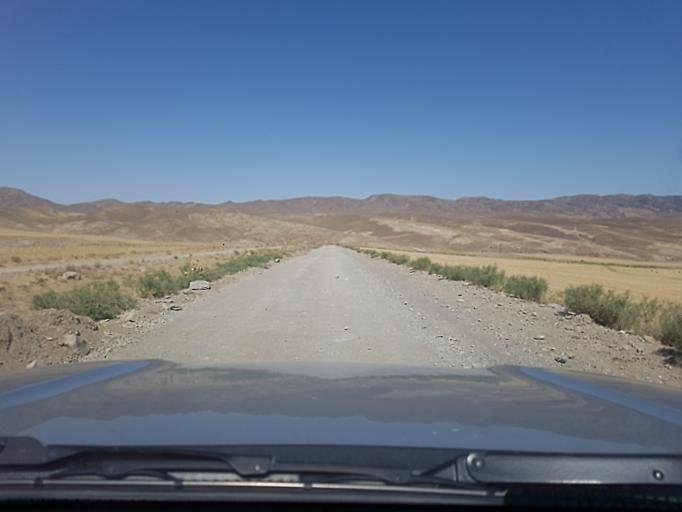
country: TM
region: Ahal
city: Baharly
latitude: 38.4116
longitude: 57.0180
